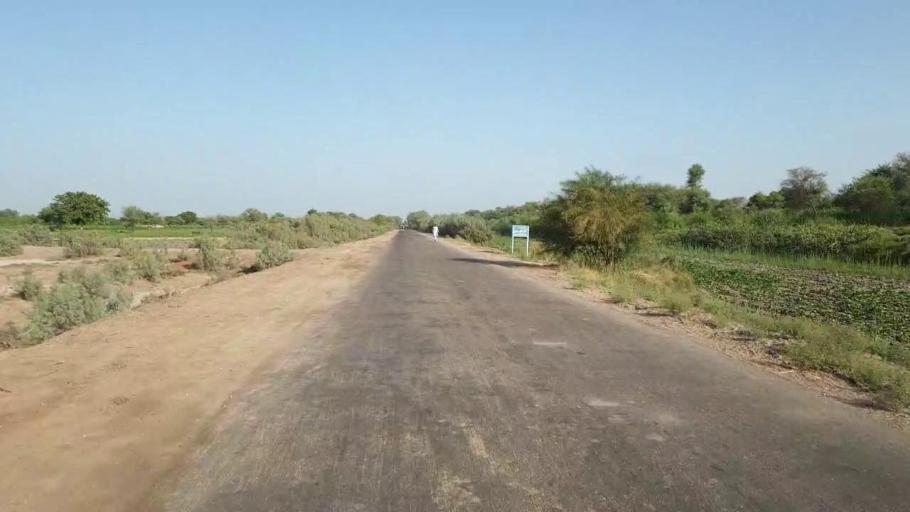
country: PK
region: Sindh
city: Nawabshah
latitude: 26.3831
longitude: 68.4562
